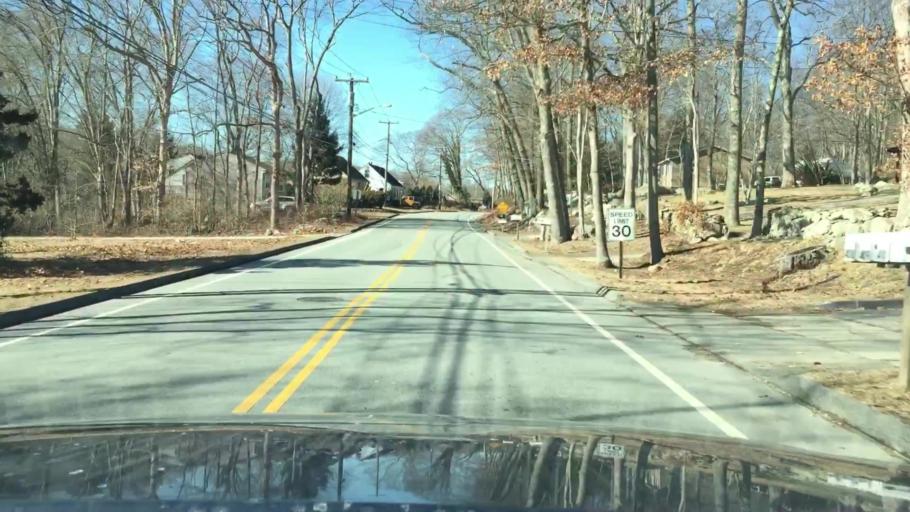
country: US
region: Connecticut
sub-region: New London County
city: Conning Towers-Nautilus Park
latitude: 41.3732
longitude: -72.0565
